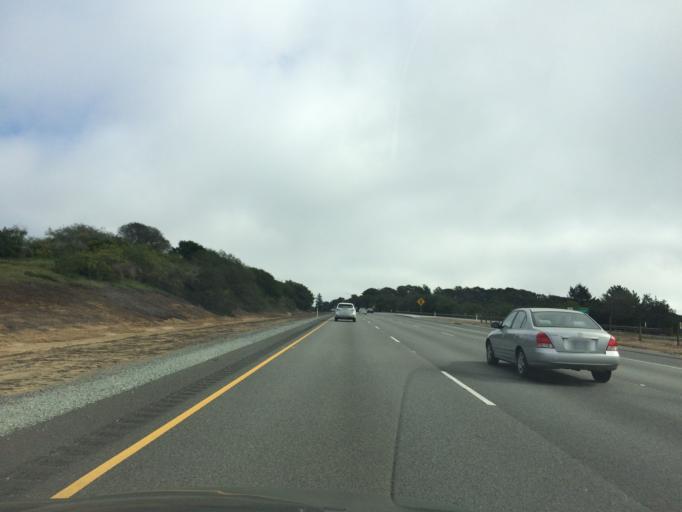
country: US
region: California
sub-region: Santa Cruz County
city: Aptos Hills-Larkin Valley
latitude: 36.9413
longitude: -121.8397
